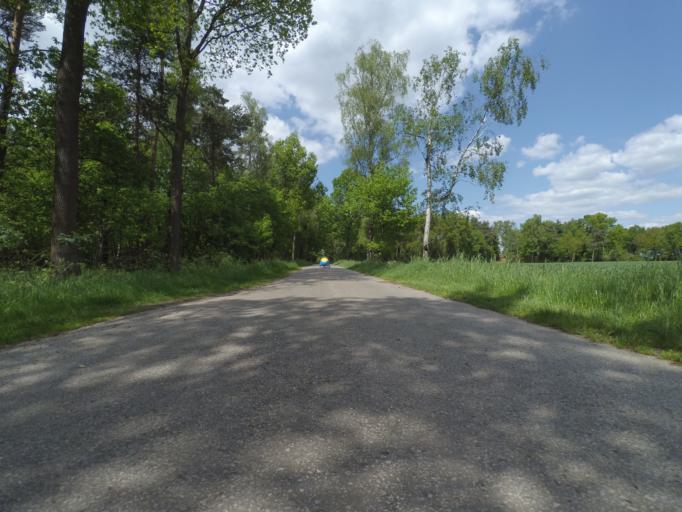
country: DE
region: Lower Saxony
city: Steinhorst
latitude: 52.6426
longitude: 10.3847
